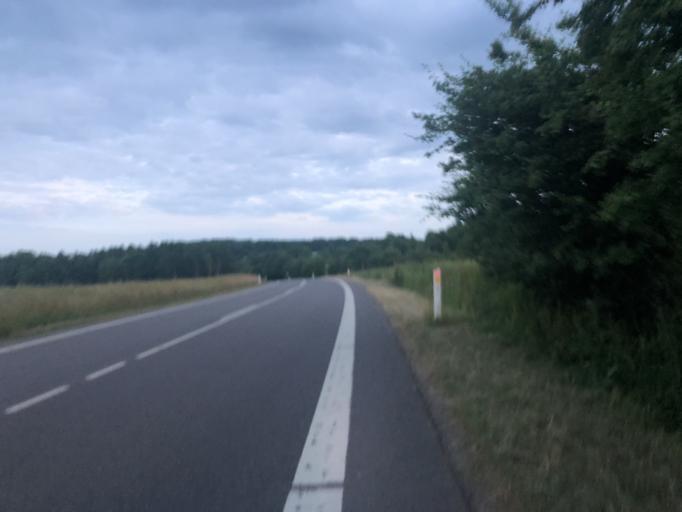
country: DK
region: Capital Region
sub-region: Bornholm Kommune
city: Akirkeby
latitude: 55.2087
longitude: 14.9368
